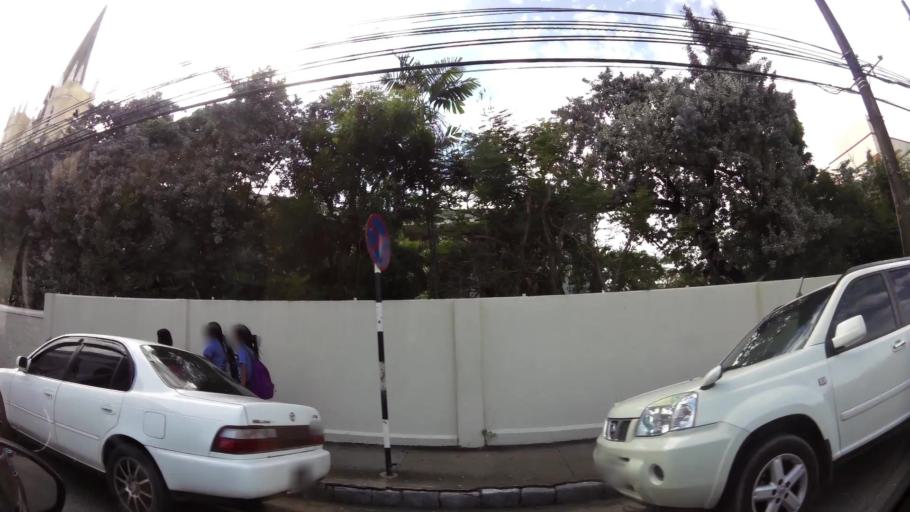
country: TT
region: City of Port of Spain
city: Port-of-Spain
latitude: 10.6594
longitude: -61.5099
